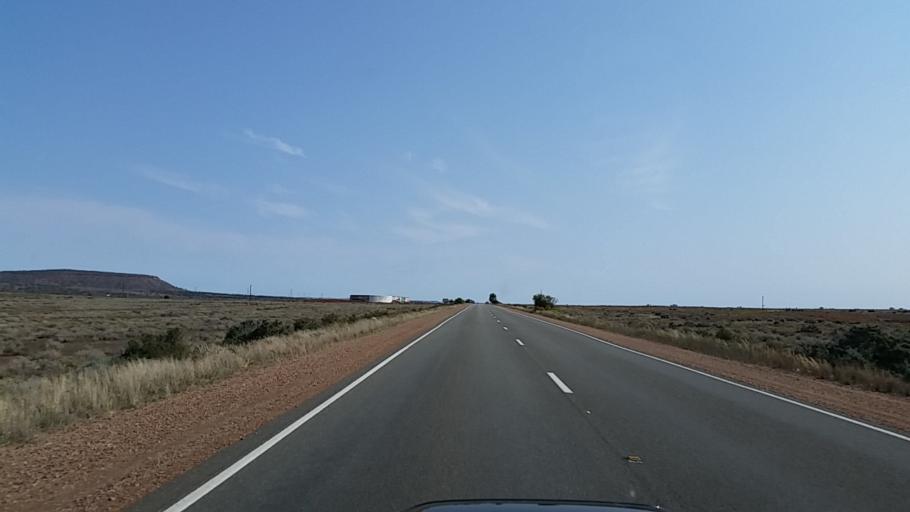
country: AU
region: South Australia
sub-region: Port Augusta
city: Port Augusta West
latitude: -32.6083
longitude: 137.5843
